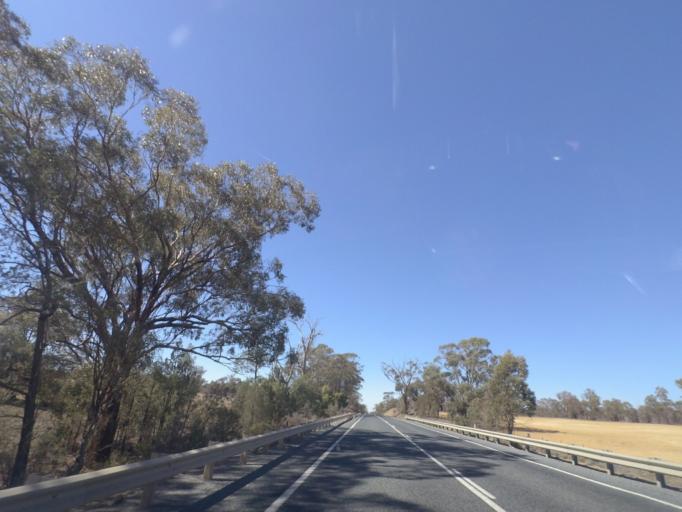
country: AU
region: New South Wales
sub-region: Bland
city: West Wyalong
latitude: -34.1652
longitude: 147.1160
